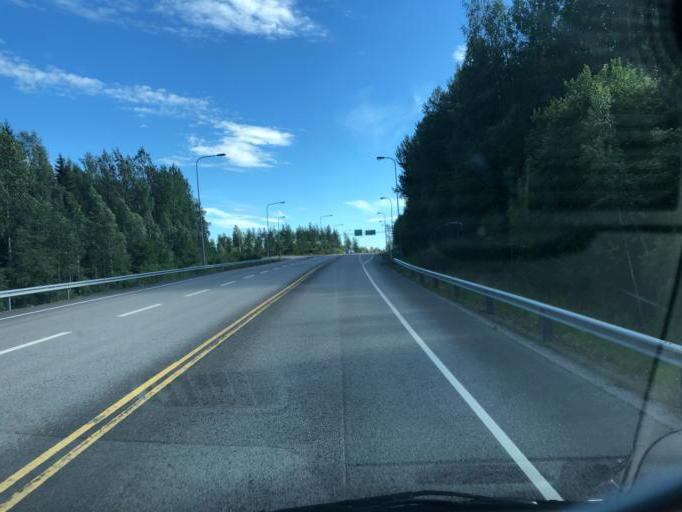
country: FI
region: Uusimaa
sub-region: Loviisa
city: Perna
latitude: 60.4962
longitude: 25.9619
